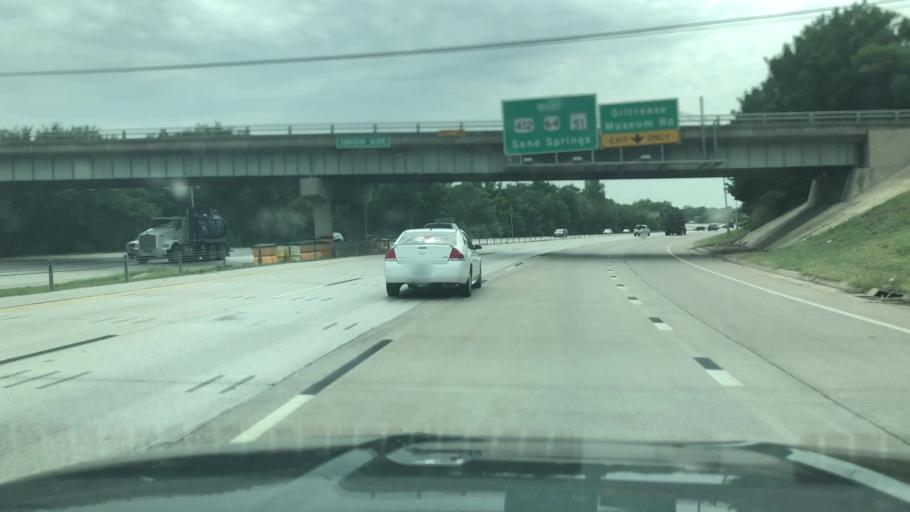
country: US
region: Oklahoma
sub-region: Tulsa County
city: Tulsa
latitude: 36.1558
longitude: -96.0110
